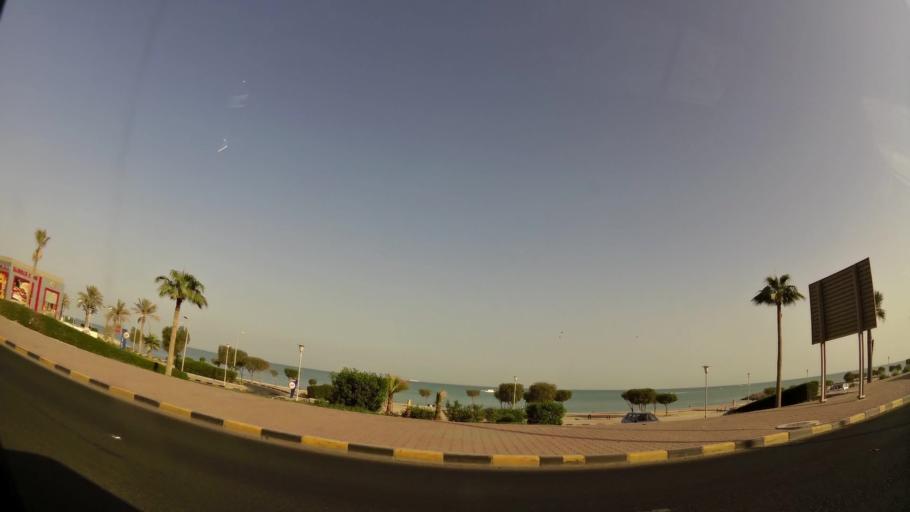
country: KW
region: Muhafazat Hawalli
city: As Salimiyah
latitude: 29.3392
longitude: 48.0956
